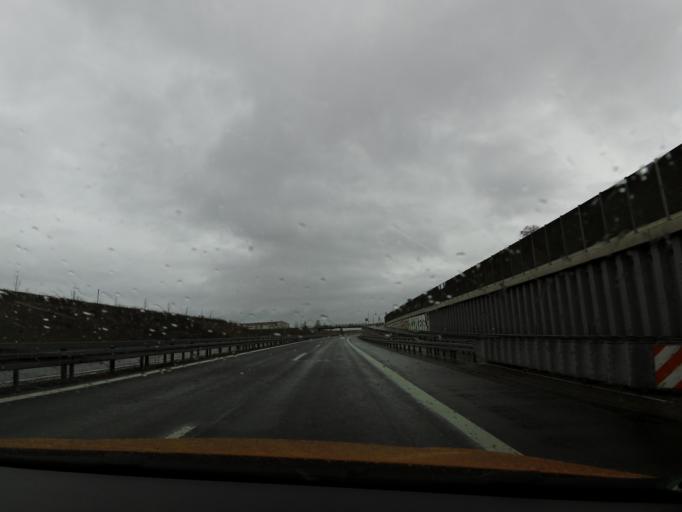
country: DE
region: Brandenburg
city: Stahnsdorf
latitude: 52.3708
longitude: 13.1963
